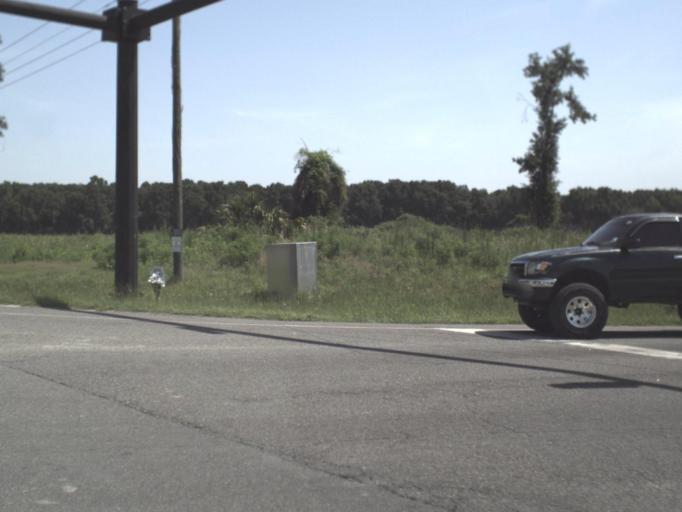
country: US
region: Florida
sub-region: Levy County
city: Chiefland
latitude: 29.5037
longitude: -82.8719
